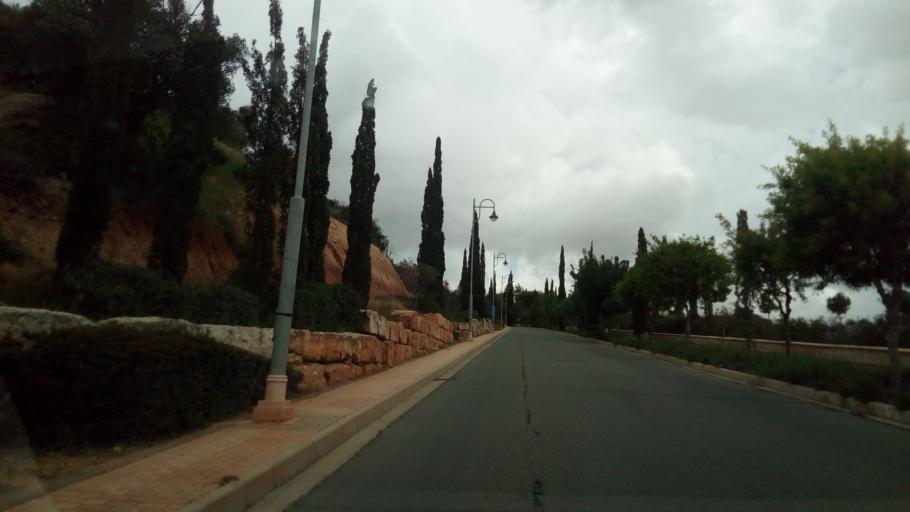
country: CY
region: Limassol
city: Pissouri
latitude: 34.6802
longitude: 32.6094
